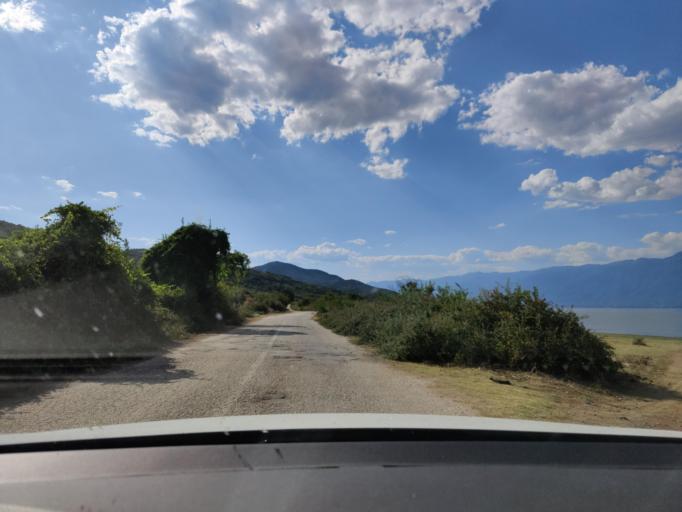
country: GR
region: Central Macedonia
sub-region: Nomos Serron
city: Chrysochorafa
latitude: 41.1528
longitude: 23.2014
